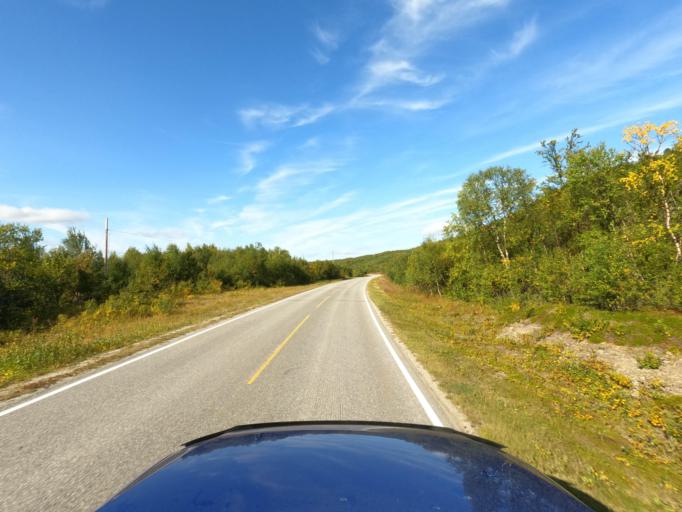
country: NO
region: Finnmark Fylke
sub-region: Porsanger
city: Lakselv
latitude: 69.7595
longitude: 25.2063
